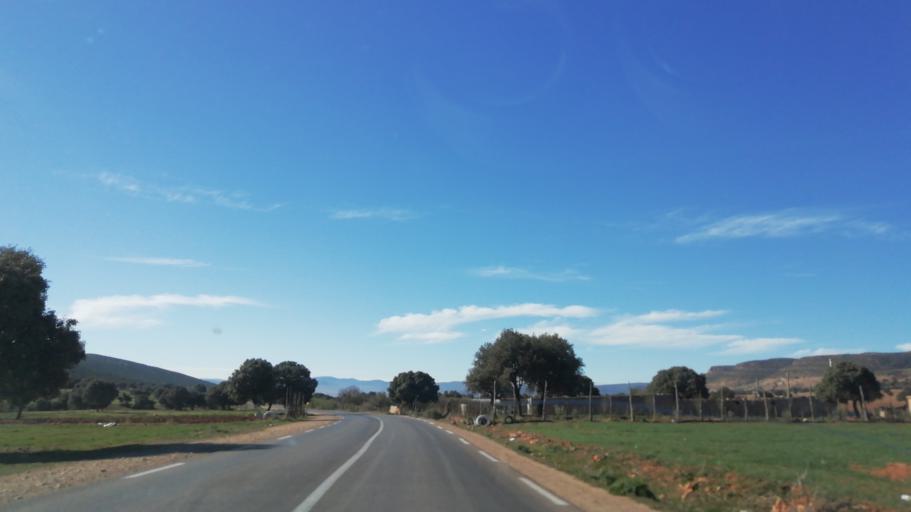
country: DZ
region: Tlemcen
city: Sebdou
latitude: 34.6969
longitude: -1.2346
